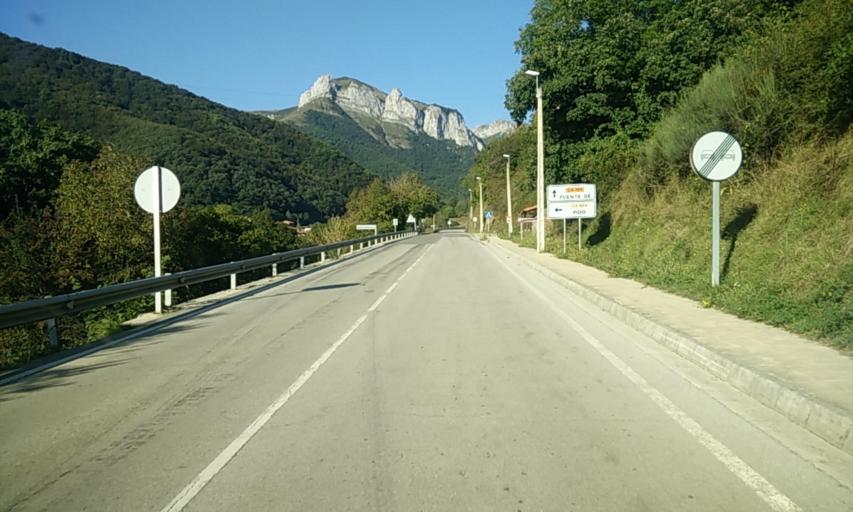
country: ES
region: Cantabria
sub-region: Provincia de Cantabria
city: Camaleno
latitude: 43.1289
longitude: -4.7906
